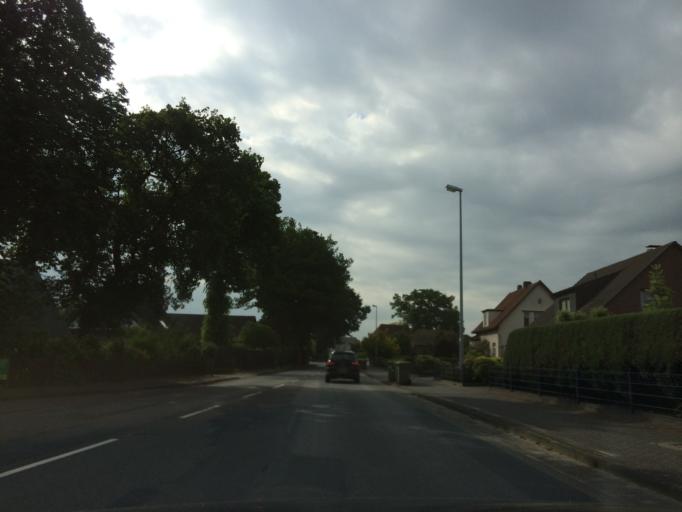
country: DE
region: Lower Saxony
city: Delmenhorst
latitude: 53.0873
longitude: 8.5843
